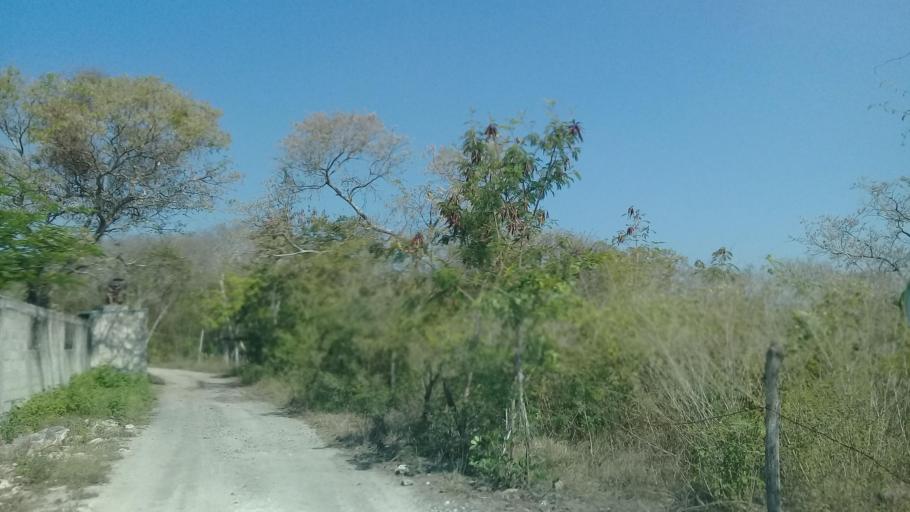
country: MX
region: Veracruz
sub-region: Emiliano Zapata
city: Plan del Rio
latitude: 19.3987
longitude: -96.6175
